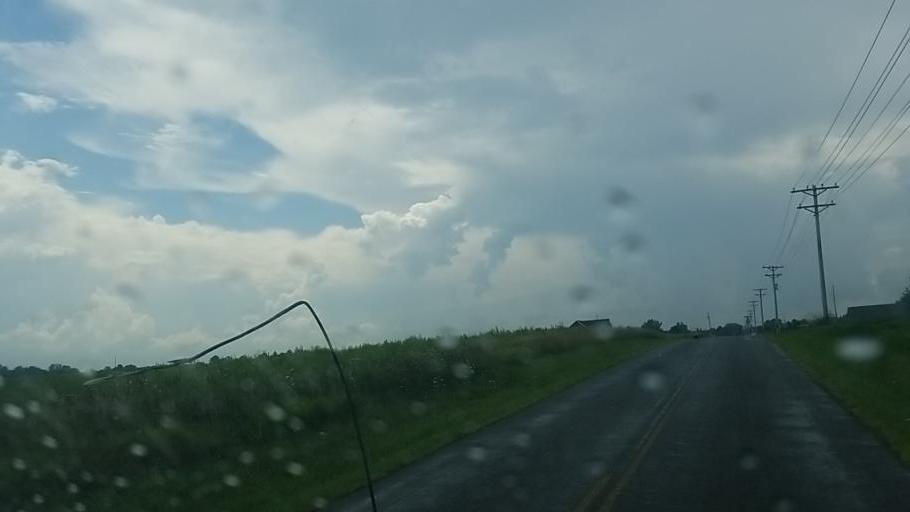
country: US
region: Ohio
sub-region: Lorain County
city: Grafton
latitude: 41.1581
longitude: -82.0117
